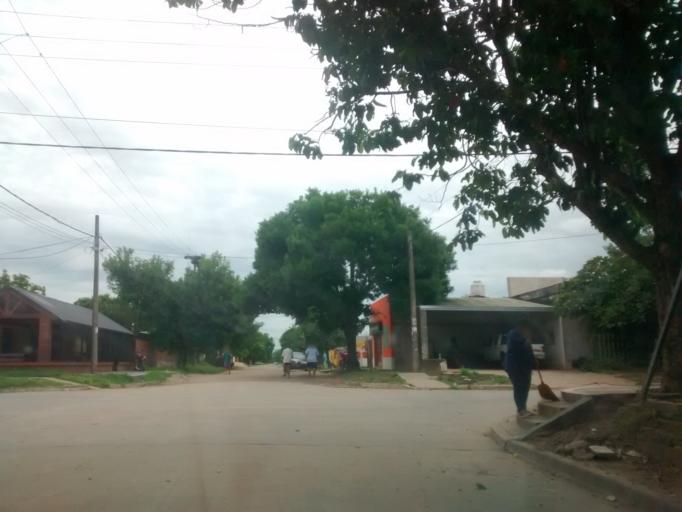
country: AR
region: Chaco
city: Puerto Tirol
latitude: -27.3721
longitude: -59.0928
